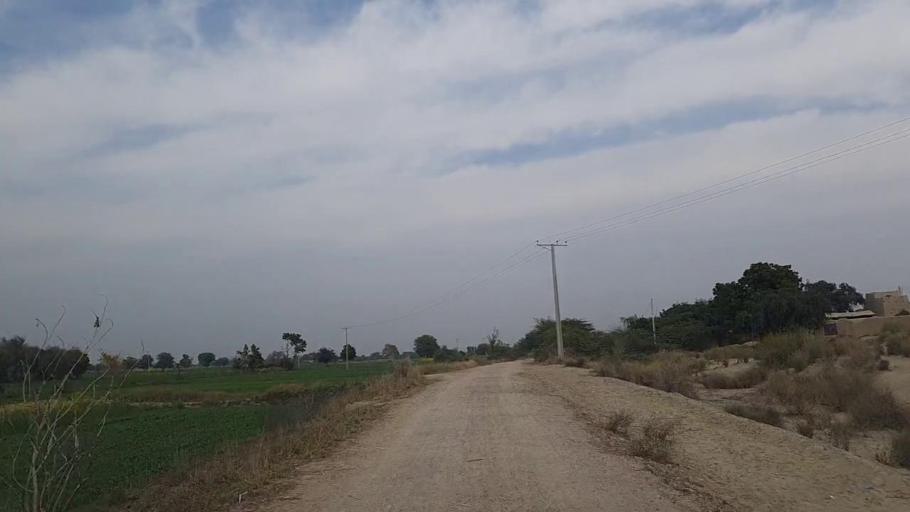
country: PK
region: Sindh
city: Daur
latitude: 26.4350
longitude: 68.4701
